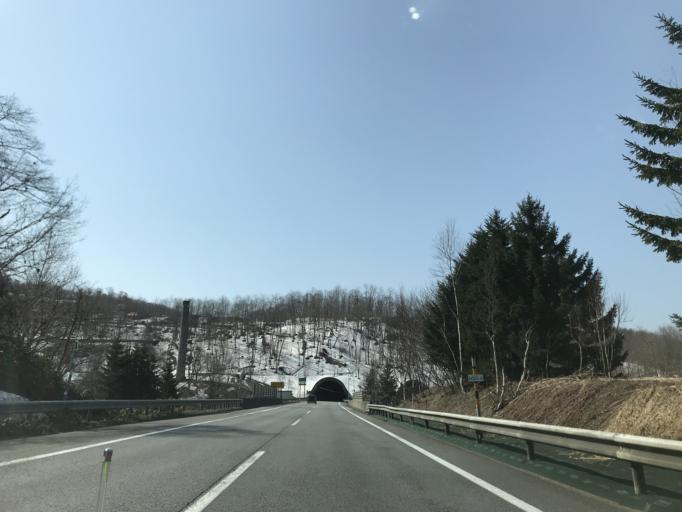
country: JP
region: Hokkaido
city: Bibai
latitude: 43.3094
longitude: 141.8817
